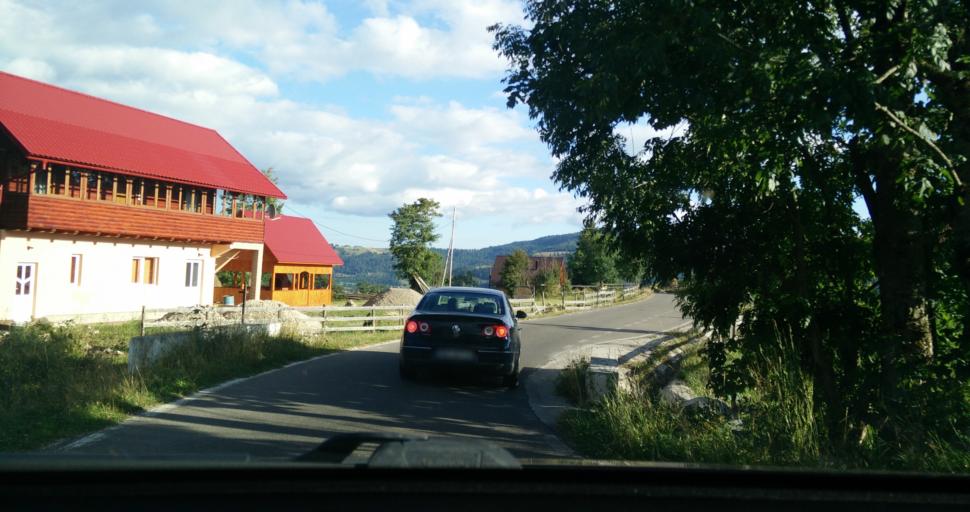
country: RO
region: Alba
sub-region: Comuna Scarisoara
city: Scarisoara
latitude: 46.4711
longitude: 22.8319
